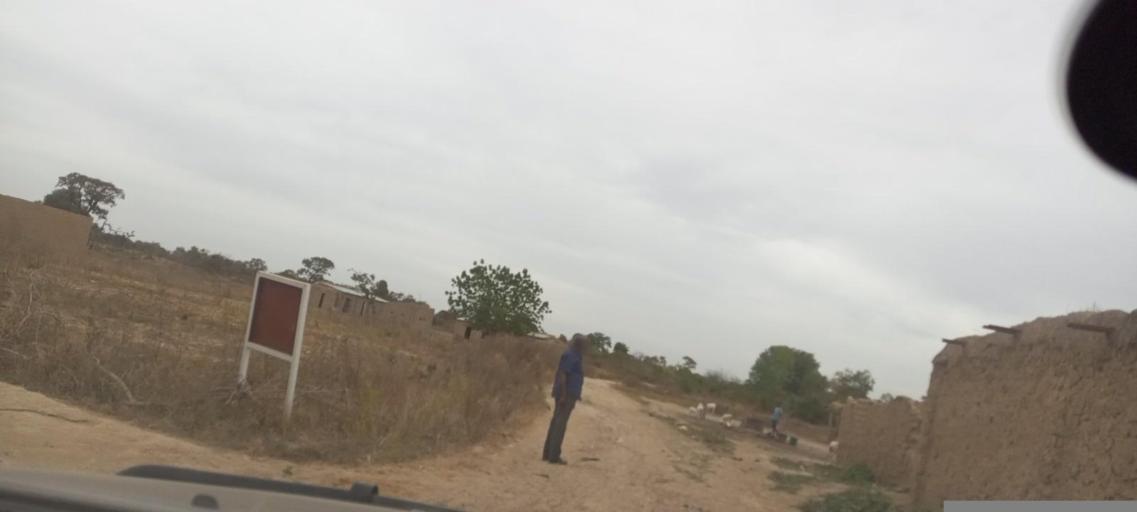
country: ML
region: Koulikoro
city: Kati
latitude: 12.7489
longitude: -8.3597
